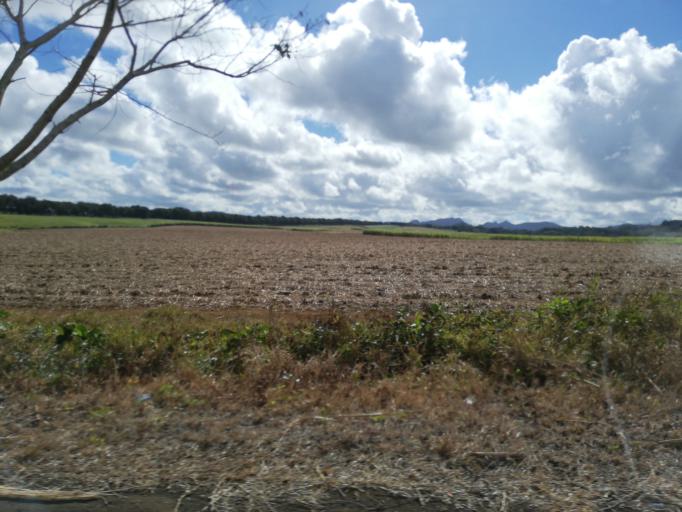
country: MU
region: Grand Port
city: Beau Vallon
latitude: -20.4043
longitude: 57.6765
